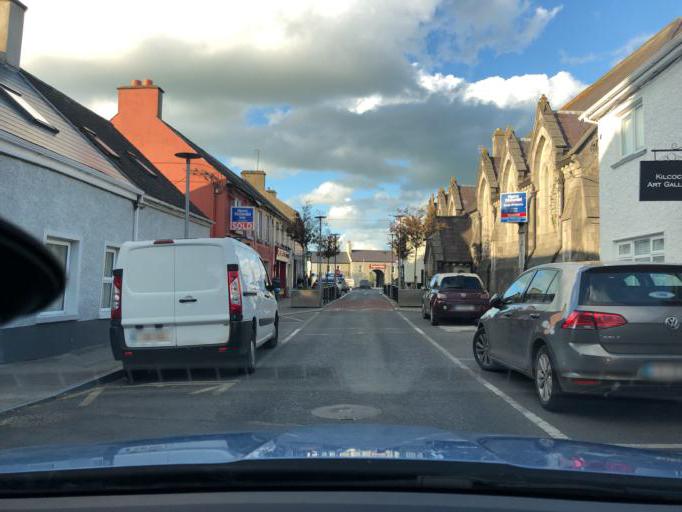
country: IE
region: Leinster
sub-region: Kildare
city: Kilcock
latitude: 53.3997
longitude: -6.6683
